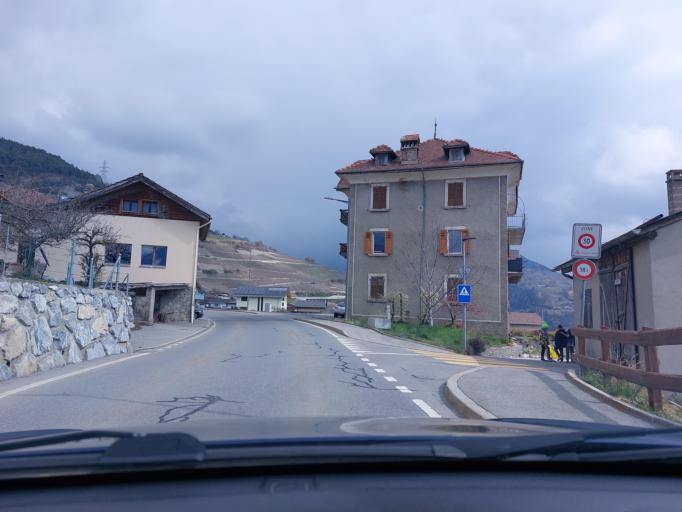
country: CH
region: Valais
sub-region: Conthey District
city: Conthey
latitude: 46.2406
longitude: 7.2956
